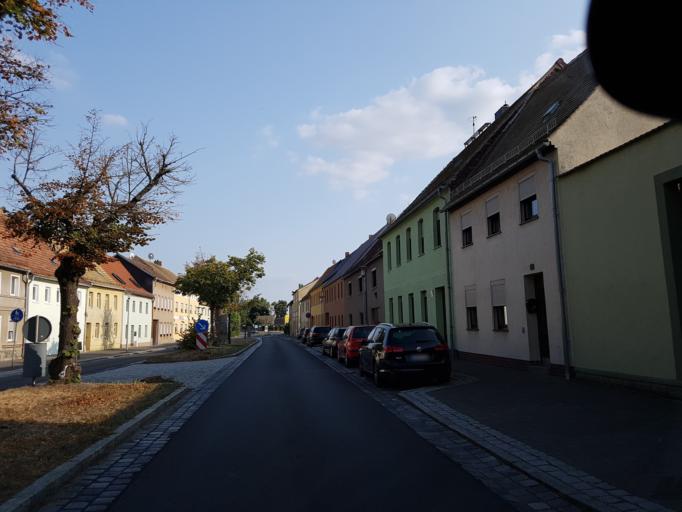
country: DE
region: Saxony
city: Dommitzsch
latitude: 51.6385
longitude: 12.8847
